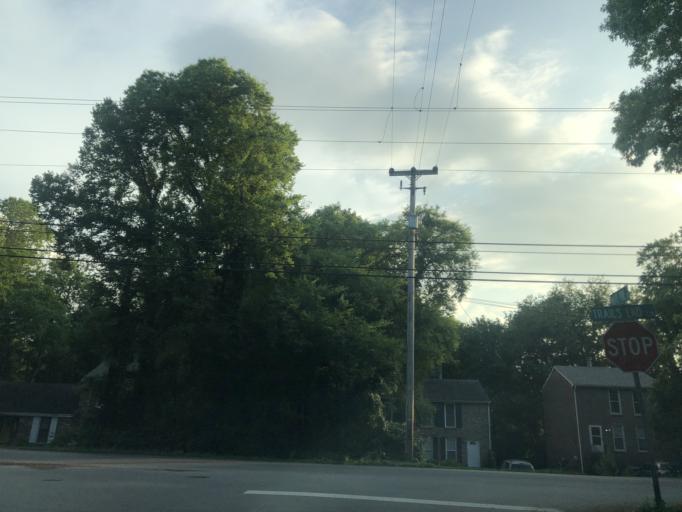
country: US
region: Tennessee
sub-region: Davidson County
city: Lakewood
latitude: 36.1394
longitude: -86.6355
